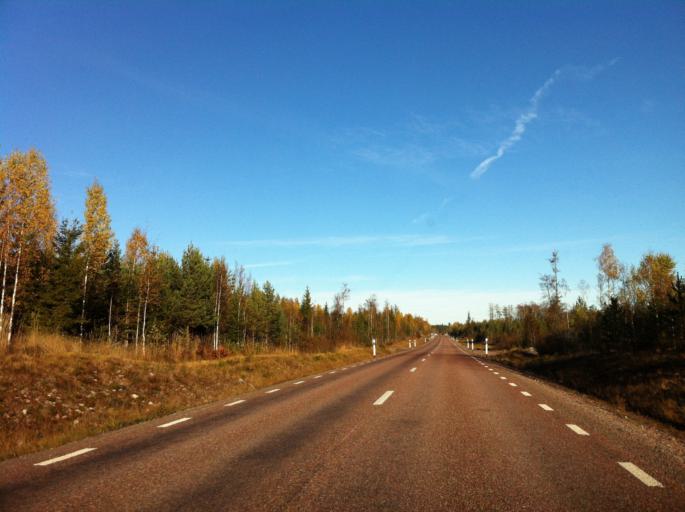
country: SE
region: Gaevleborg
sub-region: Gavle Kommun
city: Gavle
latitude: 60.6013
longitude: 17.1234
